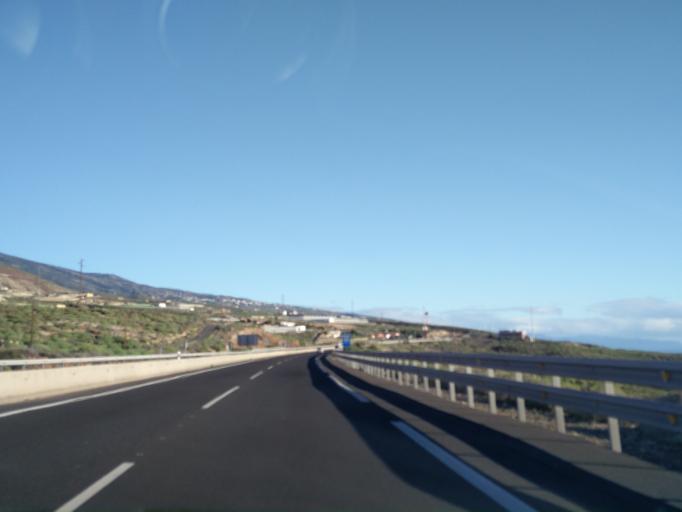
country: ES
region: Canary Islands
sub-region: Provincia de Santa Cruz de Tenerife
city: Fasnia
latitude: 28.2060
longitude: -16.4259
